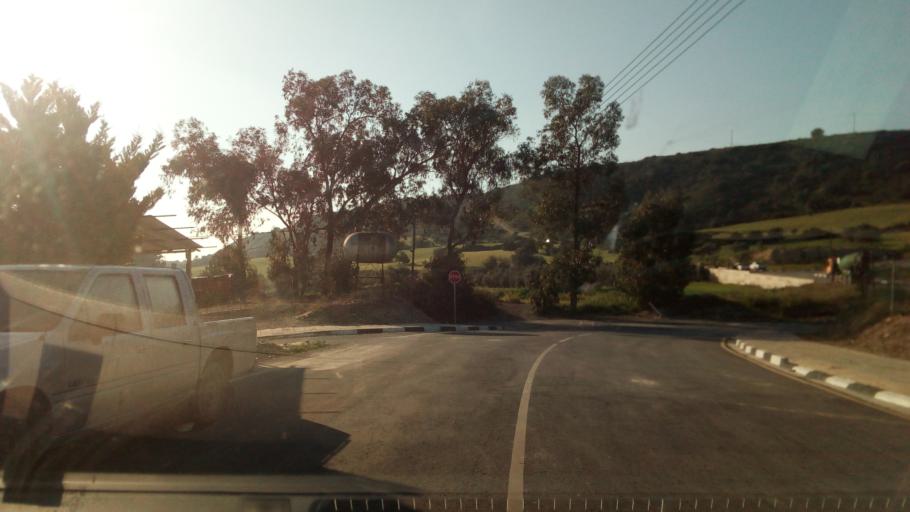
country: CY
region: Larnaka
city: Kofinou
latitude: 34.8056
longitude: 33.4338
